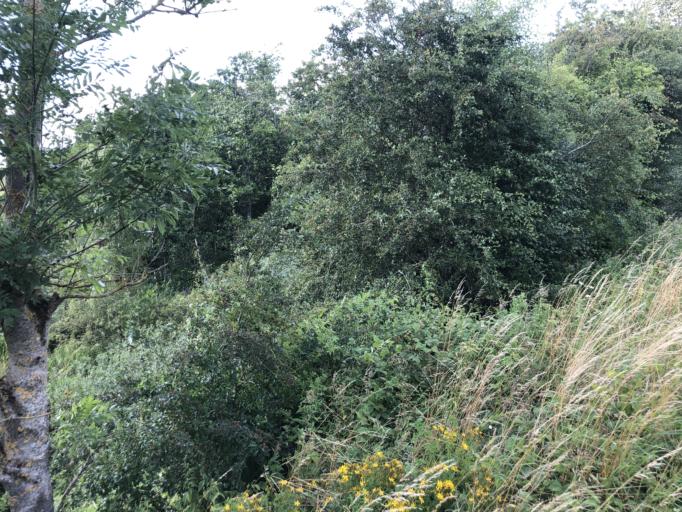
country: DK
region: South Denmark
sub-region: Vejle Kommune
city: Borkop
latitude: 55.6094
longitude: 9.6593
